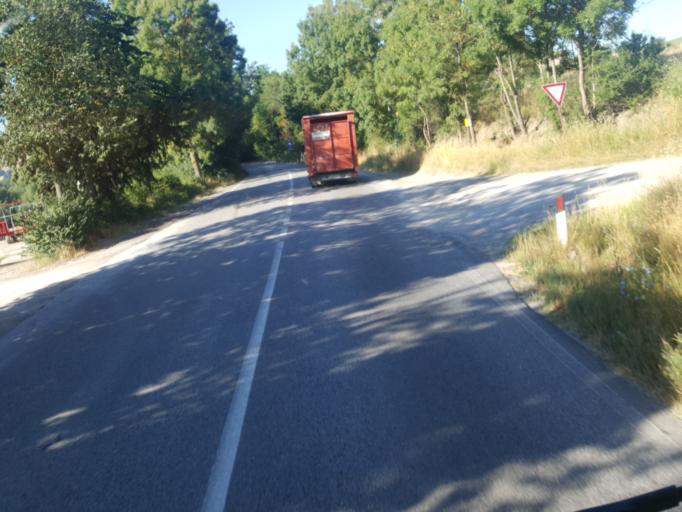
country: IT
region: The Marches
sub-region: Provincia di Pesaro e Urbino
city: Montecalvo in Foglia
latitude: 43.7980
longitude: 12.6527
